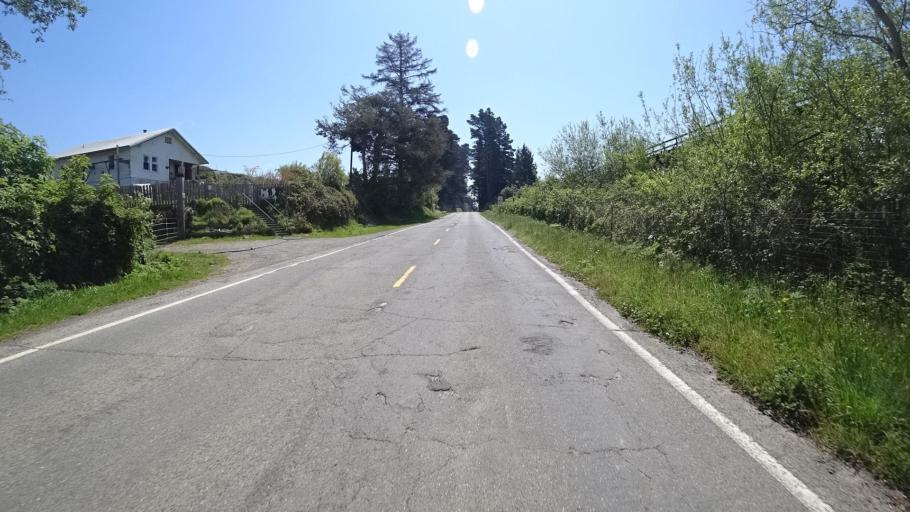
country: US
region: California
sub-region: Humboldt County
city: Ferndale
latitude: 40.6368
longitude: -124.2240
